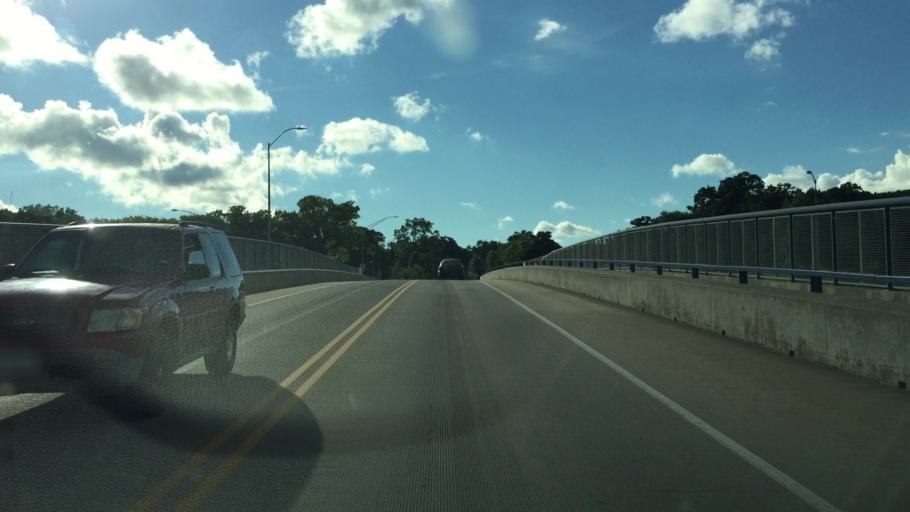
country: US
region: Iowa
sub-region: Polk County
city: Des Moines
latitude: 41.5951
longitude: -93.6475
